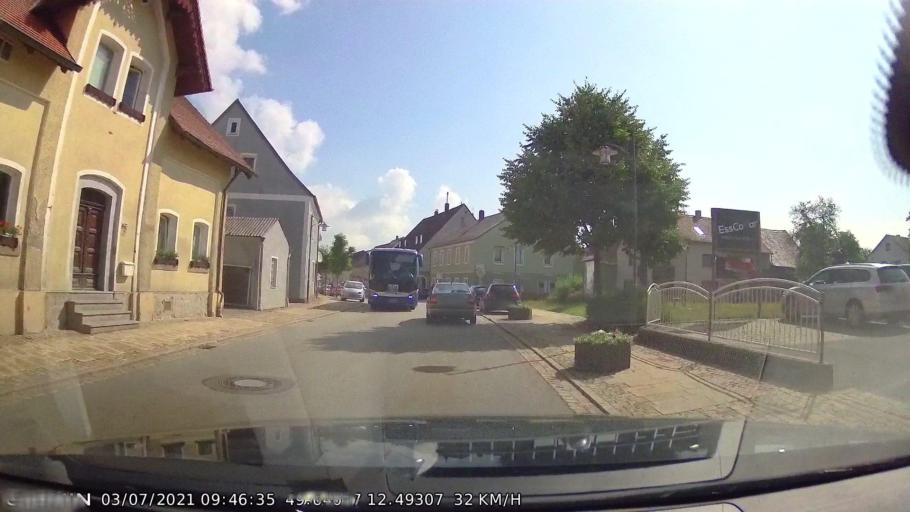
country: DE
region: Bavaria
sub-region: Upper Palatinate
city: Waidhaus
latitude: 49.6406
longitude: 12.4932
